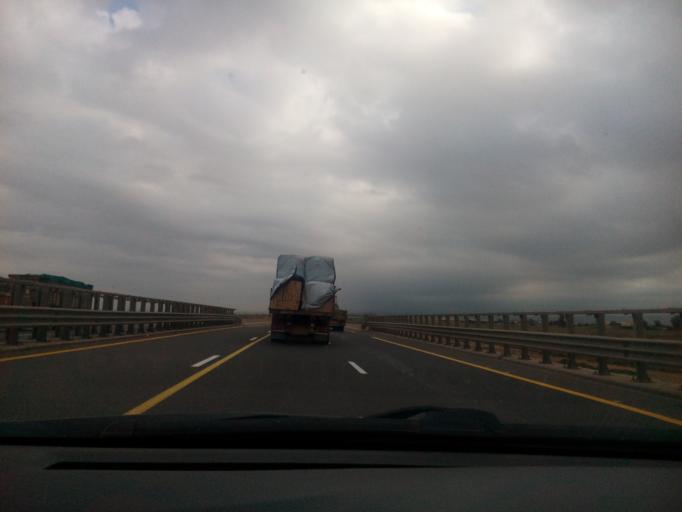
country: DZ
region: Relizane
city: Relizane
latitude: 35.7983
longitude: 0.5121
